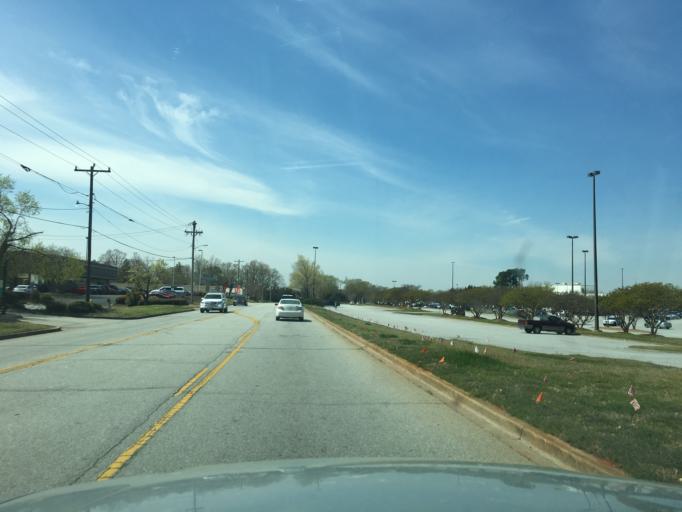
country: US
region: South Carolina
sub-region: Greenville County
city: Wade Hampton
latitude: 34.8487
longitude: -82.3302
